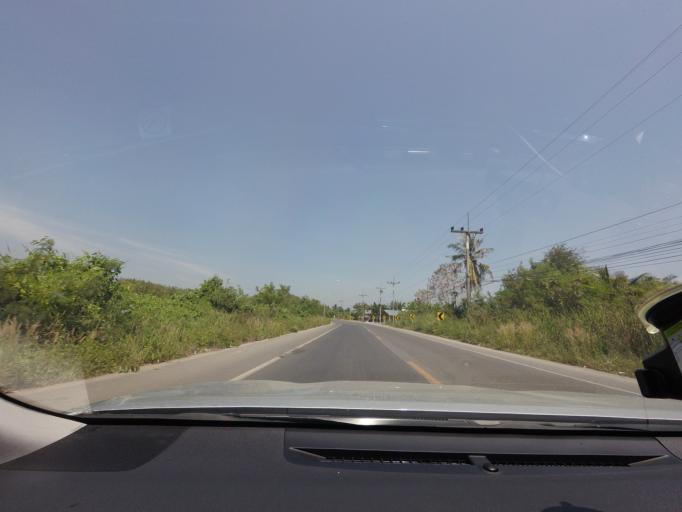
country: TH
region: Surat Thani
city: Tha Chang
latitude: 9.2095
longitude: 99.2373
